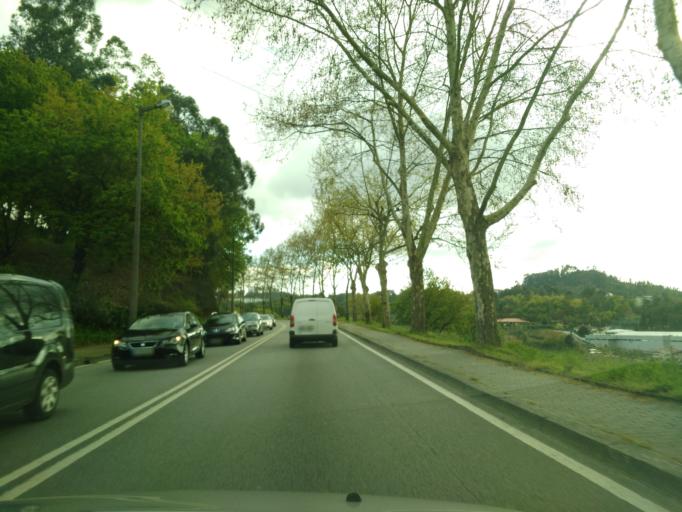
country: PT
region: Braga
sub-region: Guimaraes
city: Urgeses
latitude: 41.4283
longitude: -8.3036
